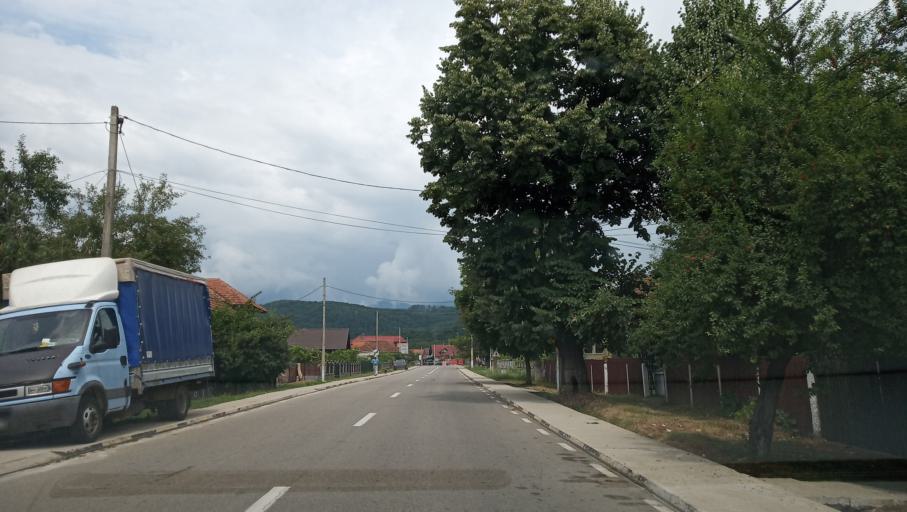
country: RO
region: Gorj
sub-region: Comuna Tismana
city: Tismana
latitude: 45.0554
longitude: 22.9456
